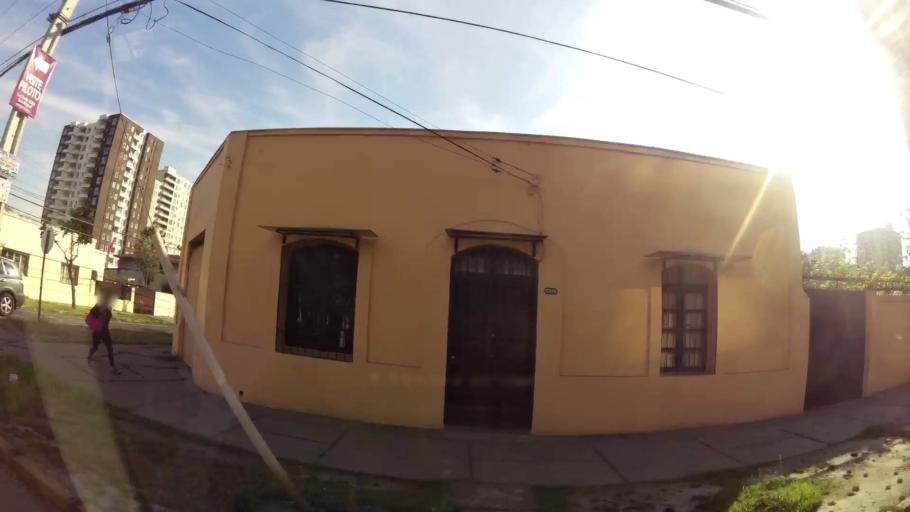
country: CL
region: Santiago Metropolitan
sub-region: Provincia de Santiago
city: Santiago
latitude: -33.5054
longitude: -70.6595
